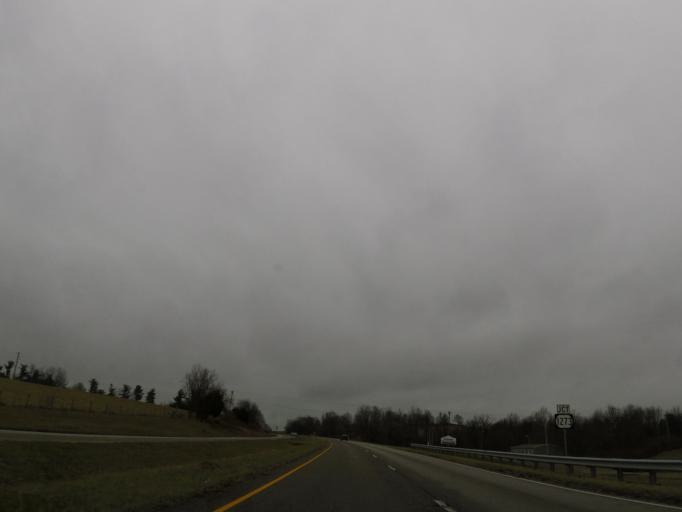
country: US
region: Kentucky
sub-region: Boyle County
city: Junction City
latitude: 37.5950
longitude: -84.7267
